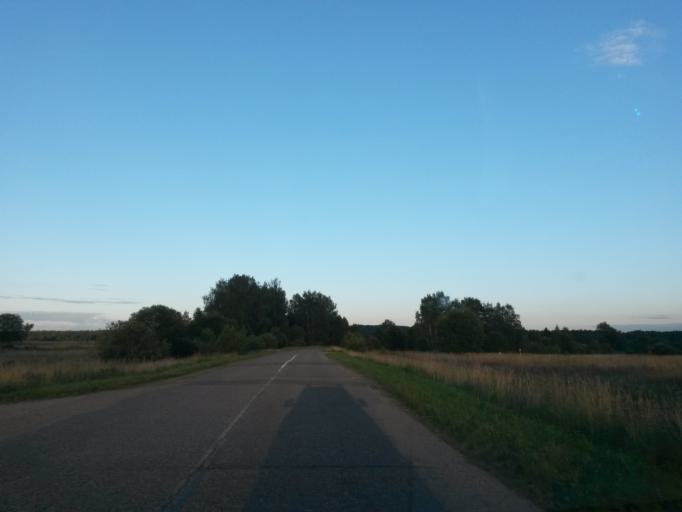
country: RU
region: Jaroslavl
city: Gavrilov-Yam
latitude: 57.3721
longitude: 40.0026
